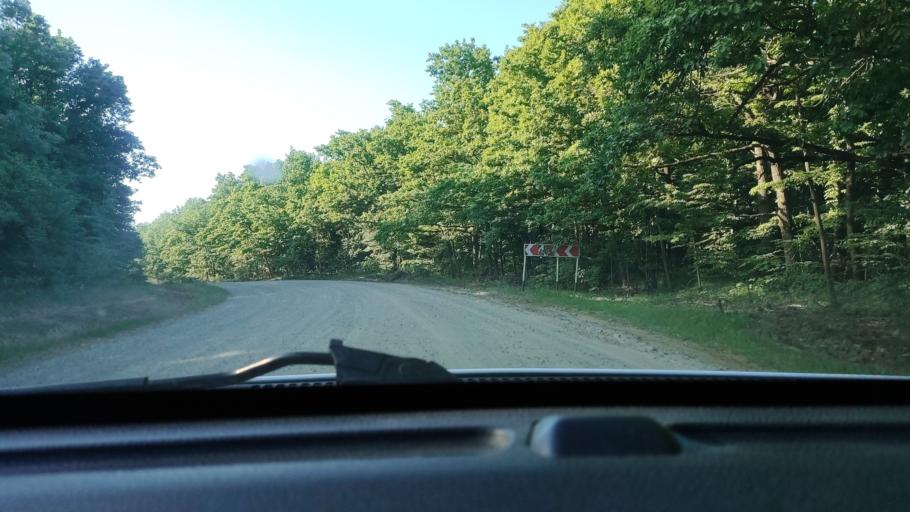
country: RU
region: Krasnodarskiy
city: Novodmitriyevskaya
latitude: 44.7178
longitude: 38.9918
